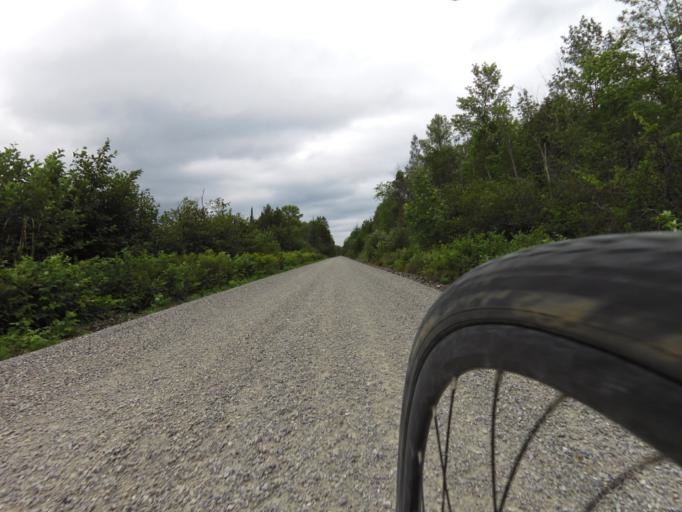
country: CA
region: Ontario
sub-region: Lanark County
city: Smiths Falls
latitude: 44.9574
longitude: -76.0483
